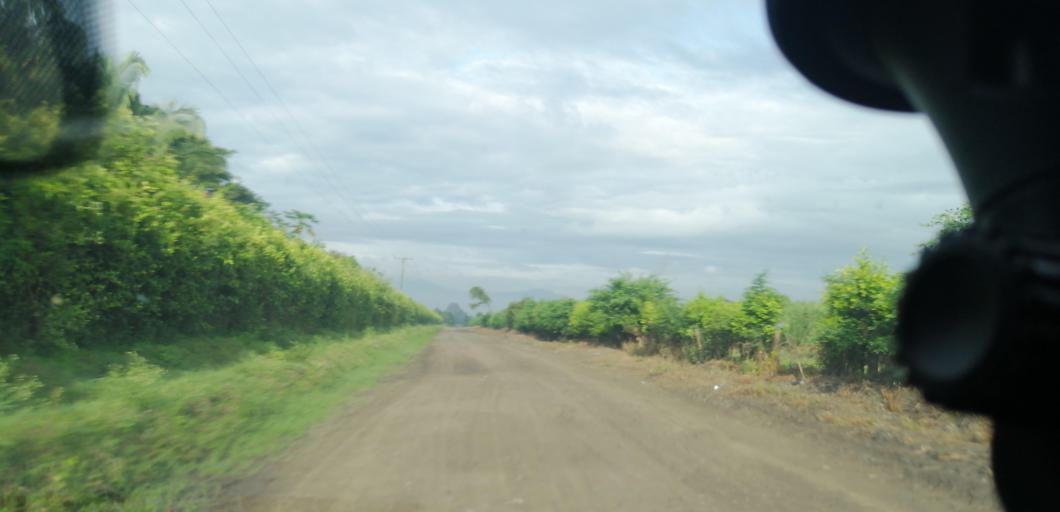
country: CO
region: Valle del Cauca
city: Palmira
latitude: 3.5532
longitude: -76.3644
